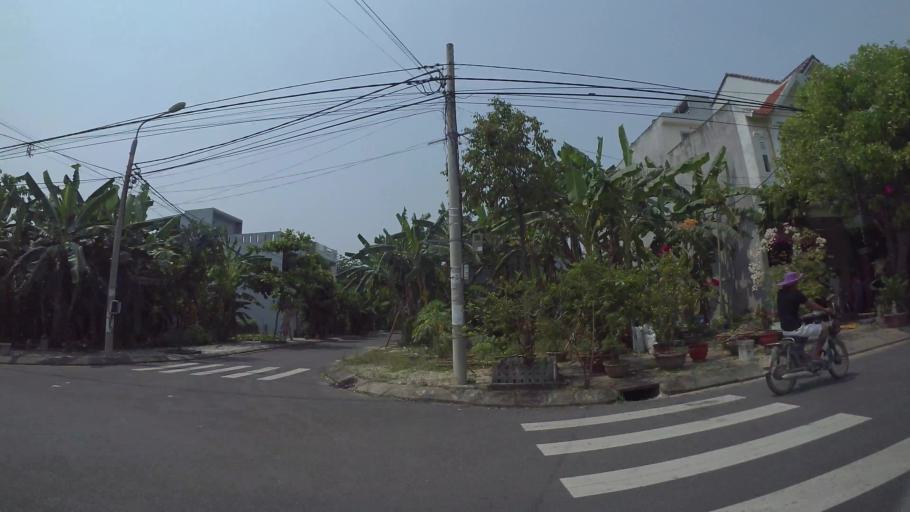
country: VN
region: Da Nang
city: Cam Le
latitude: 16.0012
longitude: 108.2193
